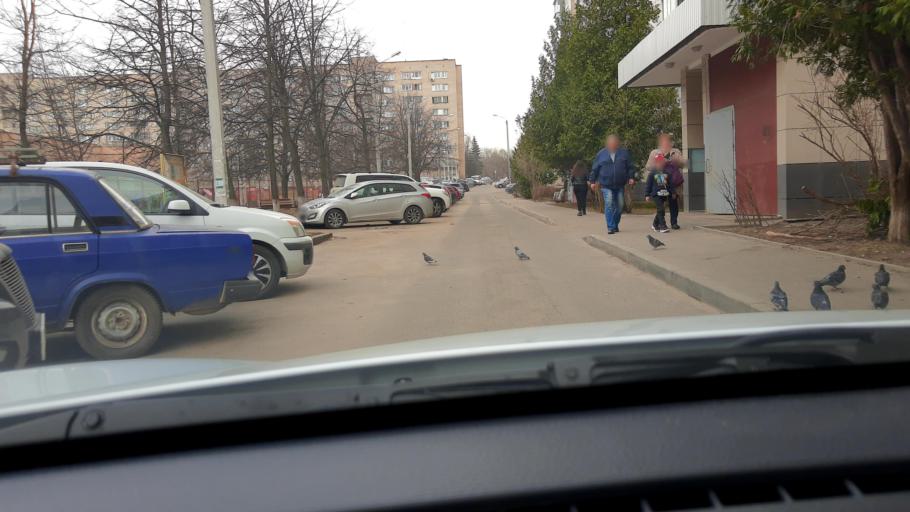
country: RU
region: Moskovskaya
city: Vostryakovo
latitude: 55.4161
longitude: 37.8328
